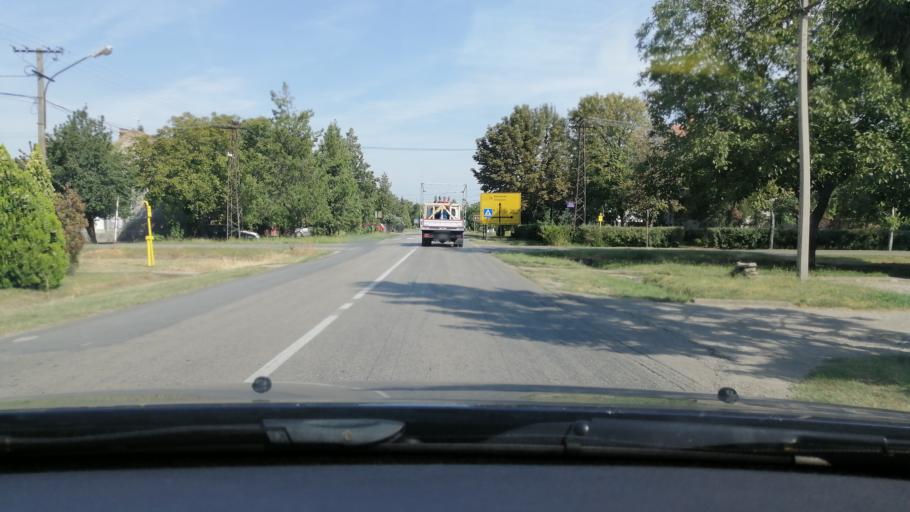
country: RS
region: Autonomna Pokrajina Vojvodina
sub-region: Juznobanatski Okrug
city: Kovacica
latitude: 45.1154
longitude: 20.6176
